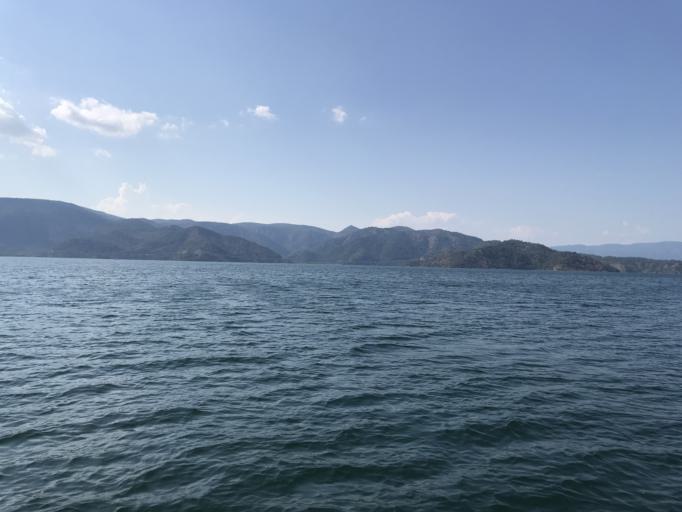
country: TR
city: Dalyan
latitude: 36.8691
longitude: 28.6184
